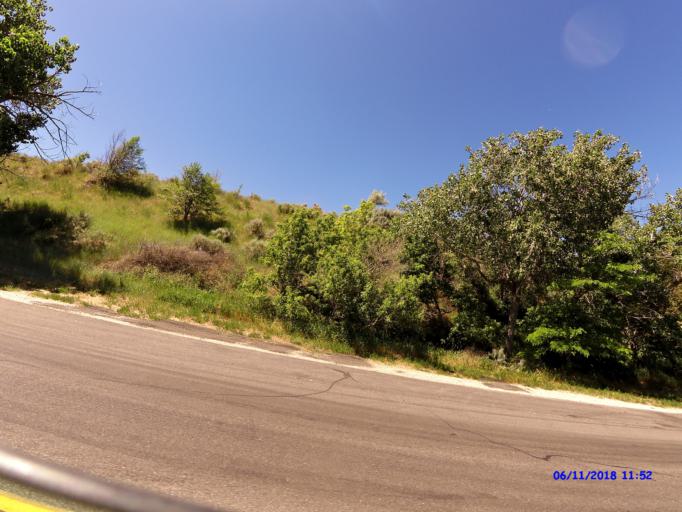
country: US
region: Utah
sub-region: Weber County
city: Ogden
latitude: 41.2348
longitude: -111.9551
